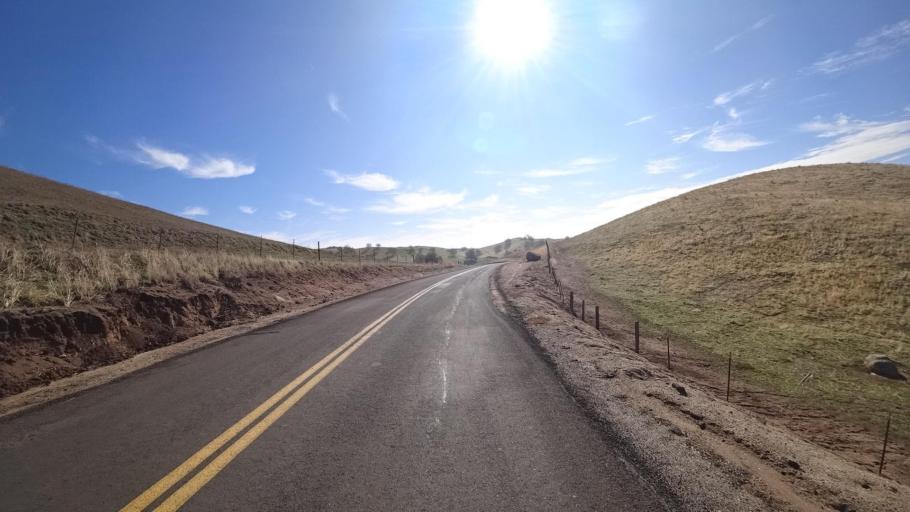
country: US
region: California
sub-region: Tulare County
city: Richgrove
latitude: 35.6874
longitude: -118.8800
